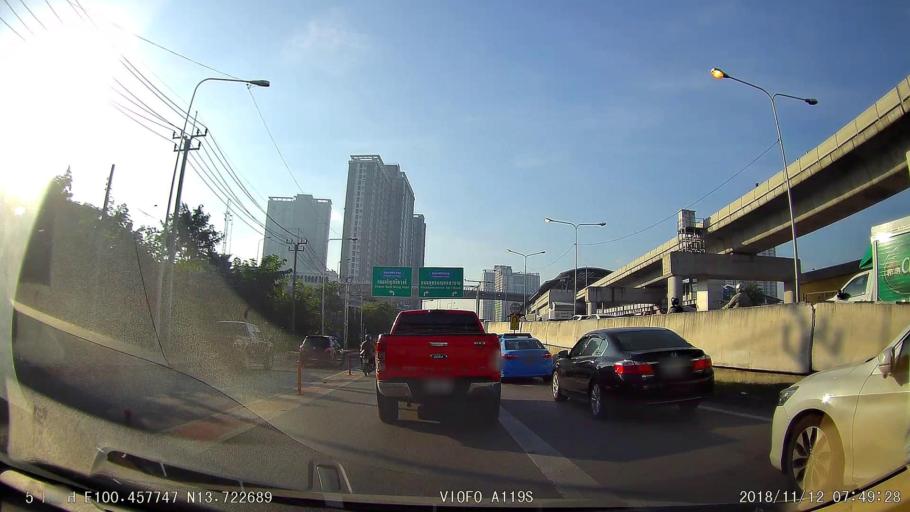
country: TH
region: Bangkok
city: Bangkok Yai
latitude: 13.7224
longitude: 100.4578
